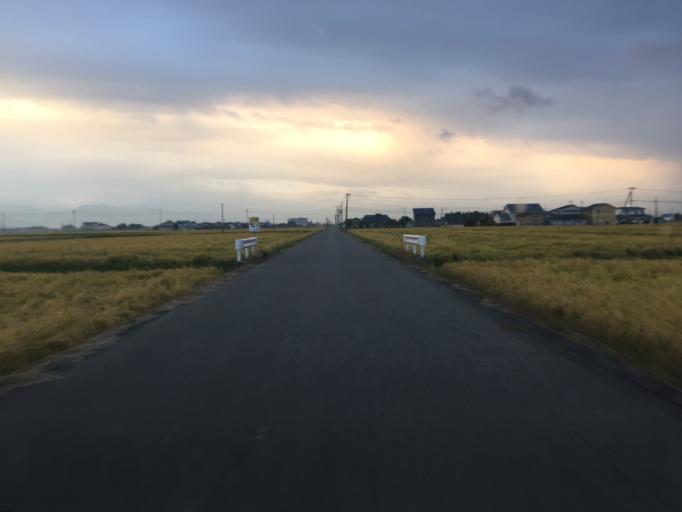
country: JP
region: Fukushima
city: Kitakata
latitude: 37.5711
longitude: 139.9069
